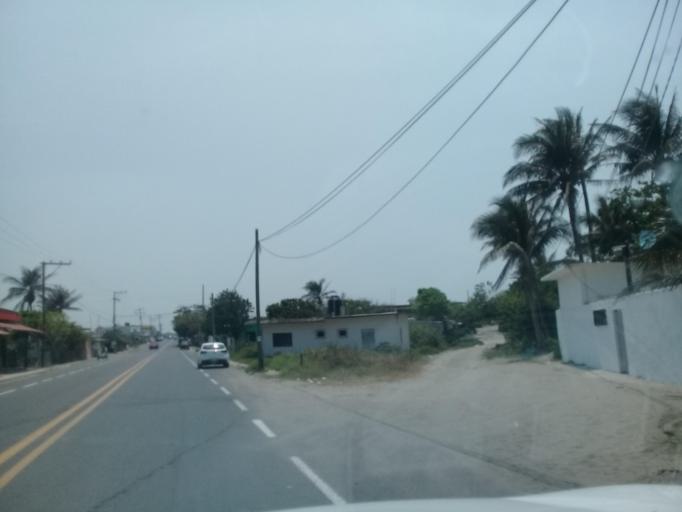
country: MX
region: Veracruz
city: Anton Lizardo
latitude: 19.0600
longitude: -95.9952
